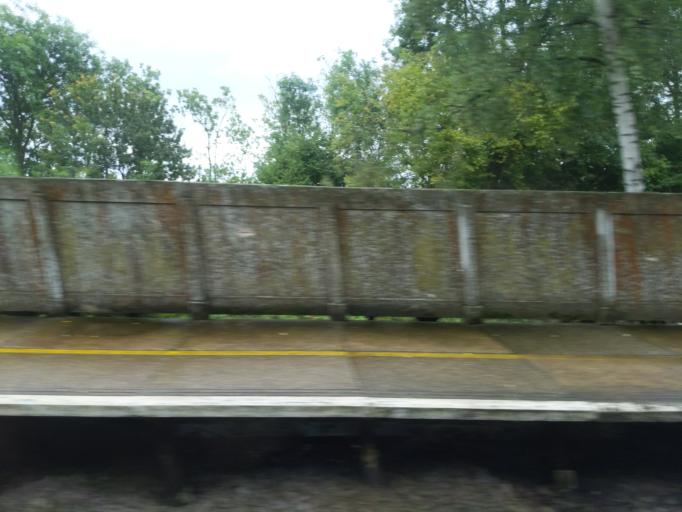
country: GB
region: England
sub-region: Kent
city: Tonbridge
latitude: 51.2141
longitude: 0.2296
